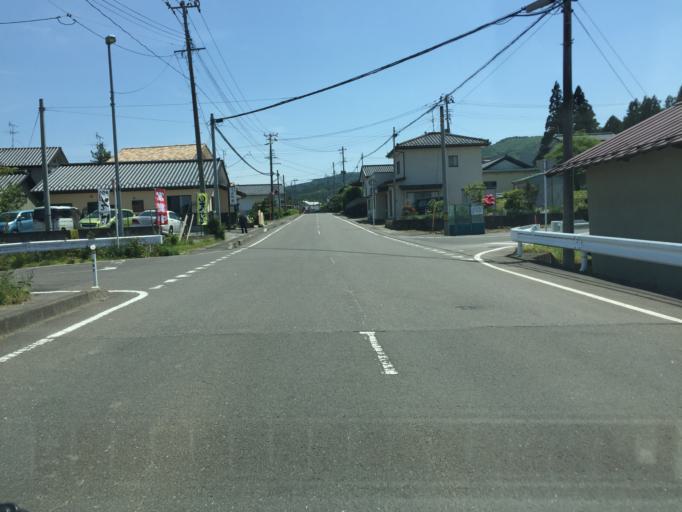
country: JP
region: Fukushima
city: Fukushima-shi
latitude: 37.7170
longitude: 140.3802
